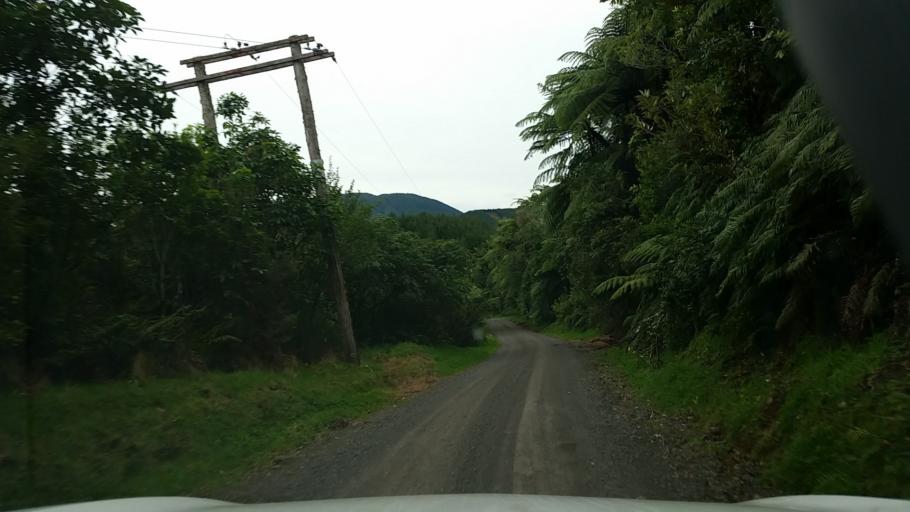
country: NZ
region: Bay of Plenty
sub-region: Rotorua District
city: Rotorua
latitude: -38.1585
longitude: 176.3636
